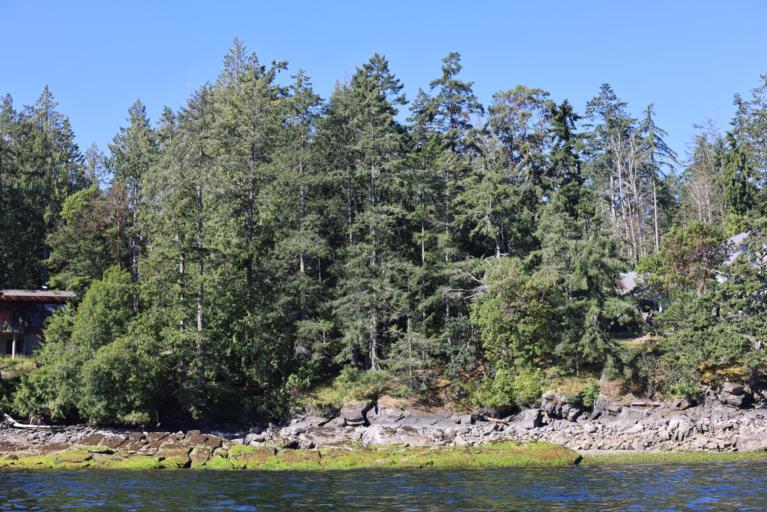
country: CA
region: British Columbia
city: North Cowichan
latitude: 48.8059
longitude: -123.5825
